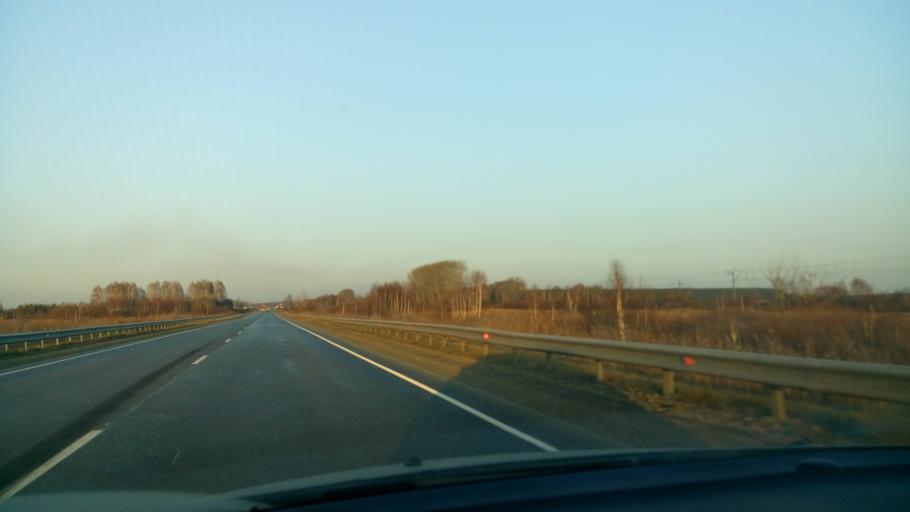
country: RU
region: Sverdlovsk
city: Obukhovskoye
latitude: 56.8306
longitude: 62.5653
